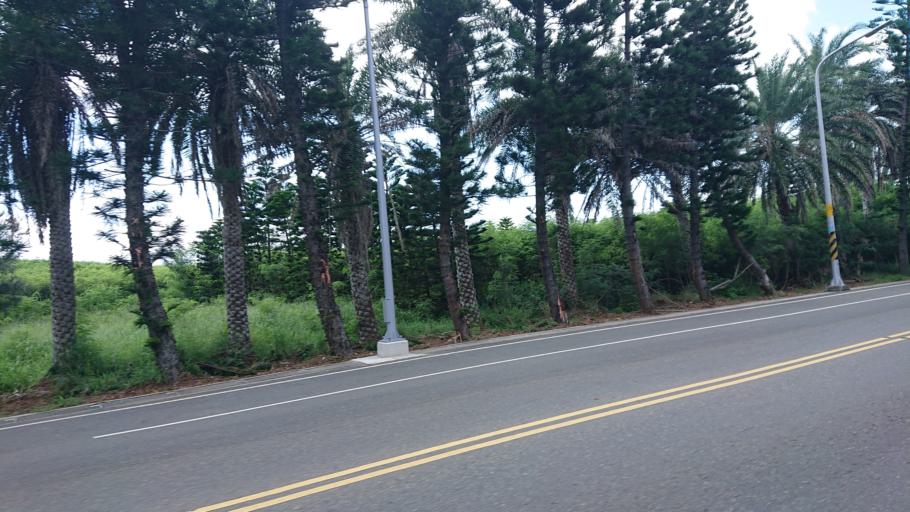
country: TW
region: Taiwan
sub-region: Penghu
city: Ma-kung
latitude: 23.5802
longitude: 119.6052
